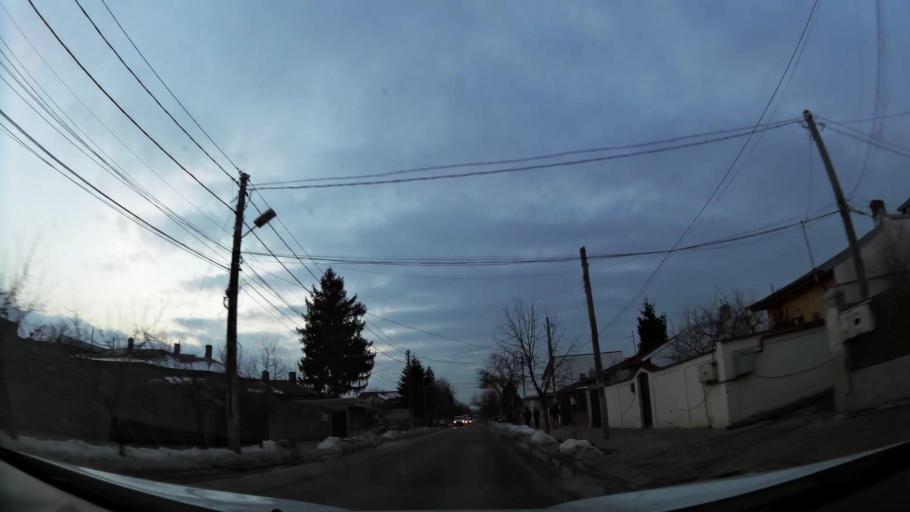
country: RO
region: Ilfov
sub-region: Comuna Popesti-Leordeni
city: Popesti-Leordeni
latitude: 44.3811
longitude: 26.1783
